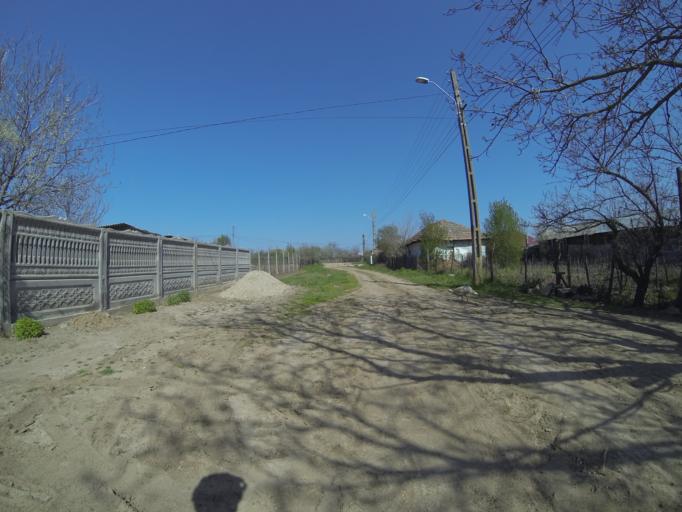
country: RO
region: Dolj
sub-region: Comuna Segarcea
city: Segarcea
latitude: 44.0919
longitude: 23.7307
